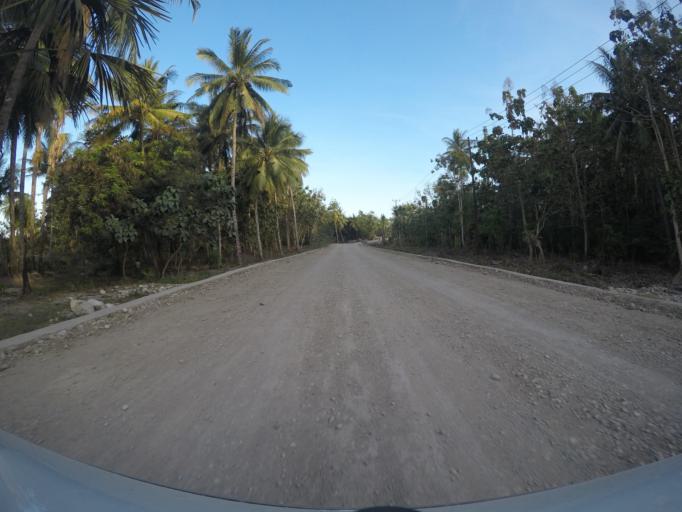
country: TL
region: Viqueque
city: Viqueque
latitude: -8.8705
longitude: 126.5073
